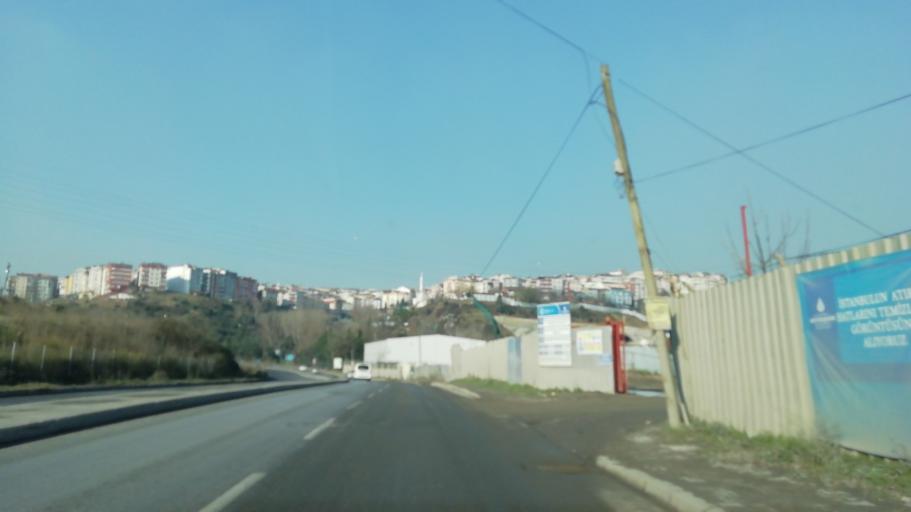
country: TR
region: Istanbul
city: Sultangazi
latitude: 41.0959
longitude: 28.9186
